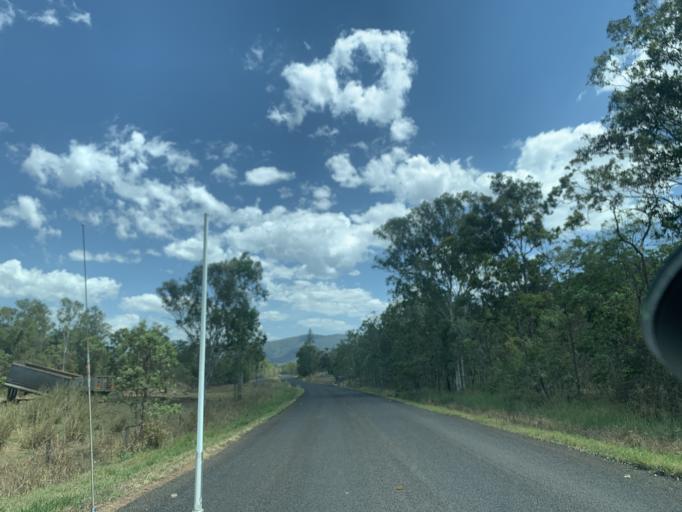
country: AU
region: Queensland
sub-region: Tablelands
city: Atherton
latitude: -17.2945
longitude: 145.4731
